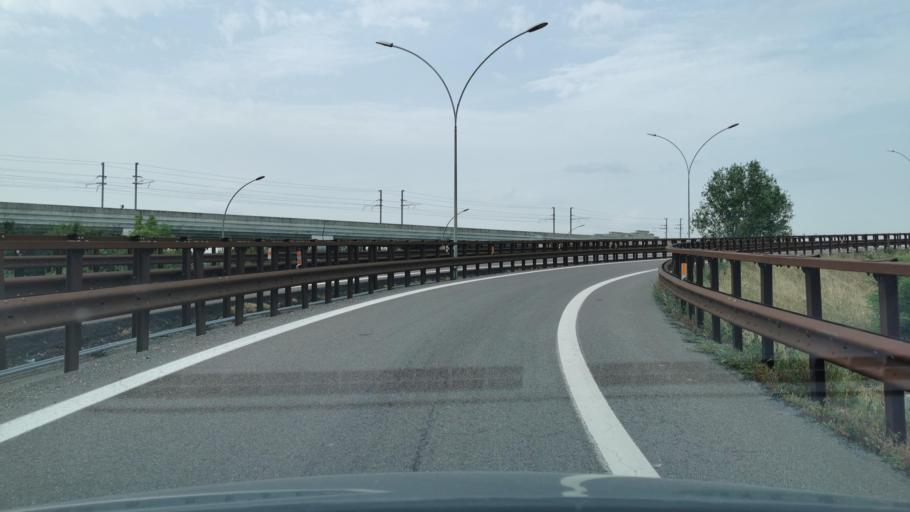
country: IT
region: Emilia-Romagna
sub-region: Provincia di Modena
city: Campogalliano
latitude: 44.6761
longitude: 10.8487
